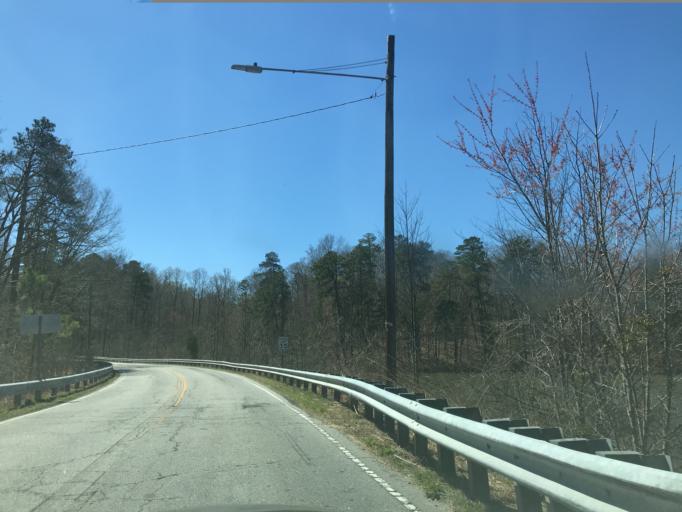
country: US
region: North Carolina
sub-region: Wake County
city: West Raleigh
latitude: 35.7615
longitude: -78.7168
